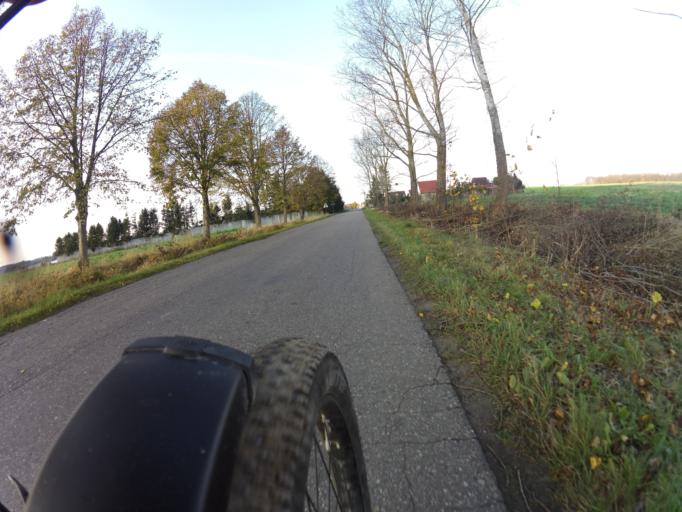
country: PL
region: Pomeranian Voivodeship
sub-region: Powiat pucki
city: Krokowa
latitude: 54.7567
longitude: 18.1842
